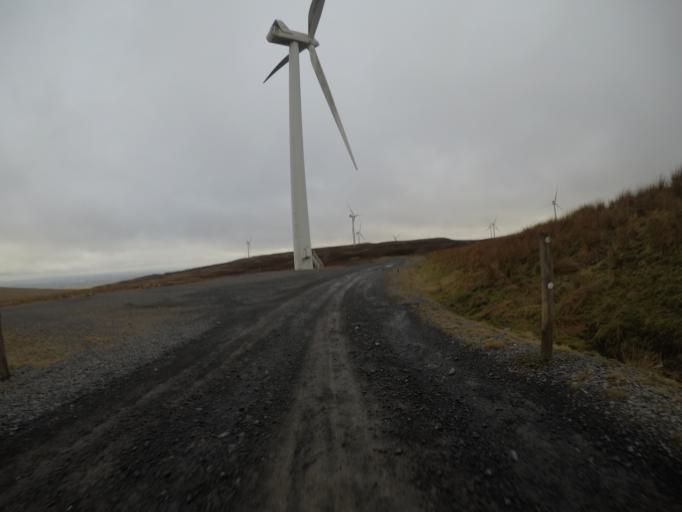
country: GB
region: Scotland
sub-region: North Ayrshire
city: Fairlie
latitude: 55.7557
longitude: -4.7945
